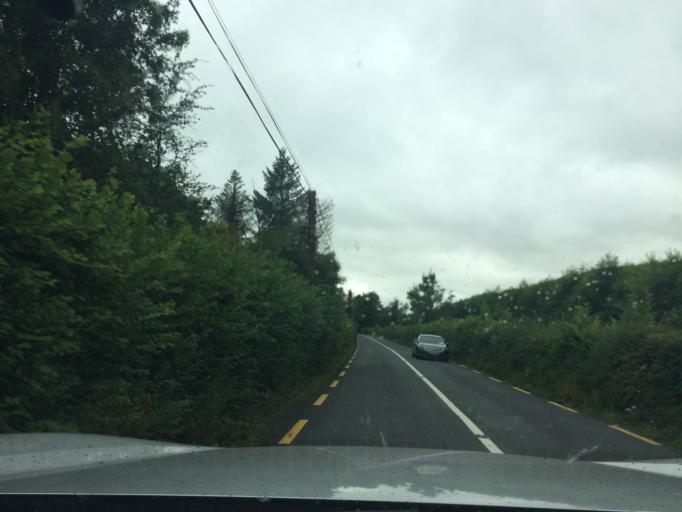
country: IE
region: Munster
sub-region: South Tipperary
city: Cluain Meala
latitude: 52.3283
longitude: -7.7393
